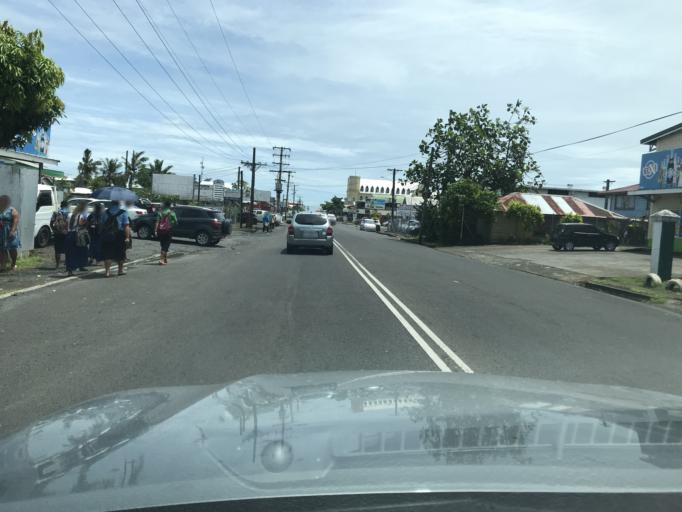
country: WS
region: Tuamasaga
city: Apia
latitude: -13.8373
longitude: -171.7711
